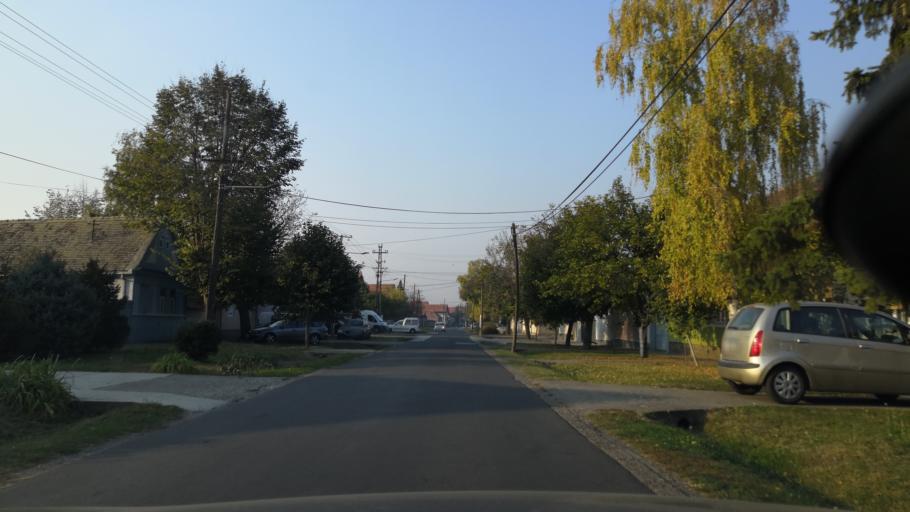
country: RS
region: Autonomna Pokrajina Vojvodina
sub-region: Sremski Okrug
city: Stara Pazova
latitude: 44.9937
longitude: 20.1466
